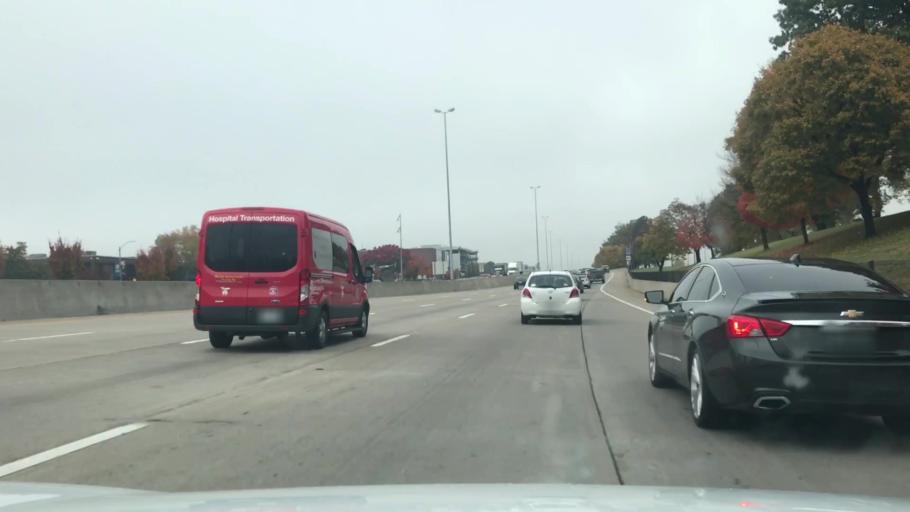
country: US
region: Missouri
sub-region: Saint Louis County
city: University City
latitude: 38.6299
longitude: -90.2714
